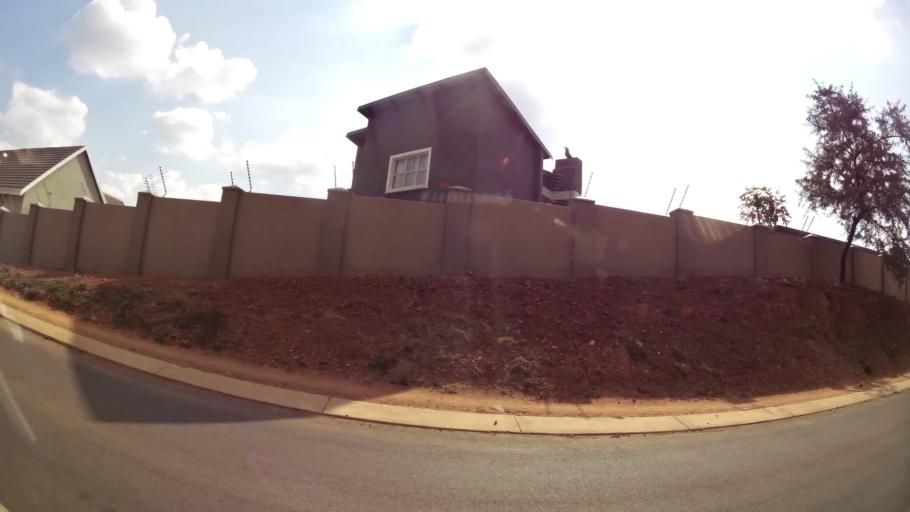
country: ZA
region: Gauteng
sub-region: City of Tshwane Metropolitan Municipality
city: Centurion
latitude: -25.8107
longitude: 28.3449
